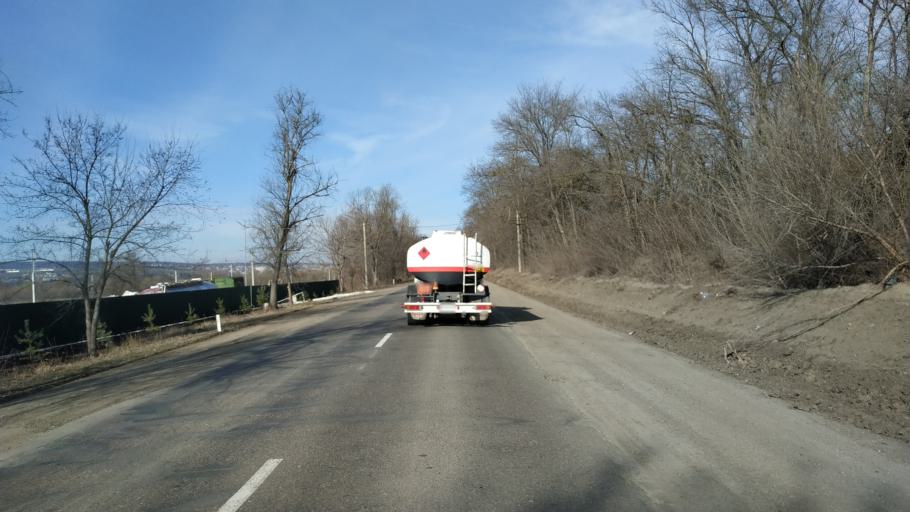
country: MD
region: Laloveni
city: Ialoveni
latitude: 46.9543
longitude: 28.7560
